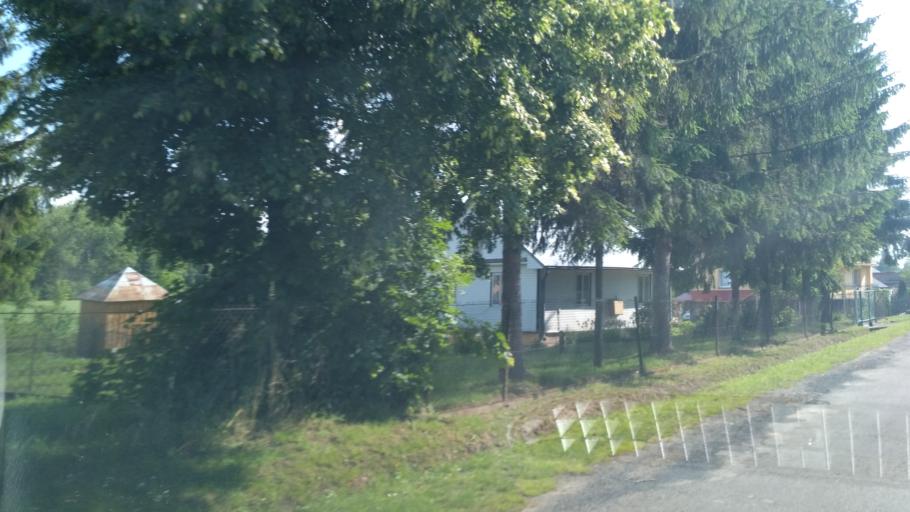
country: PL
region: Subcarpathian Voivodeship
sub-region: Powiat jaroslawski
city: Rokietnica
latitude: 49.9243
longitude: 22.6891
